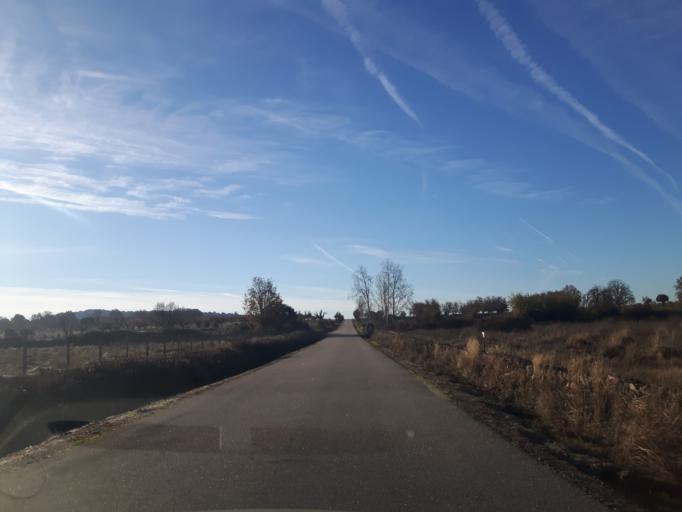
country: ES
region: Castille and Leon
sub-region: Provincia de Salamanca
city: Olmedo de Camaces
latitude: 40.9156
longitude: -6.6174
